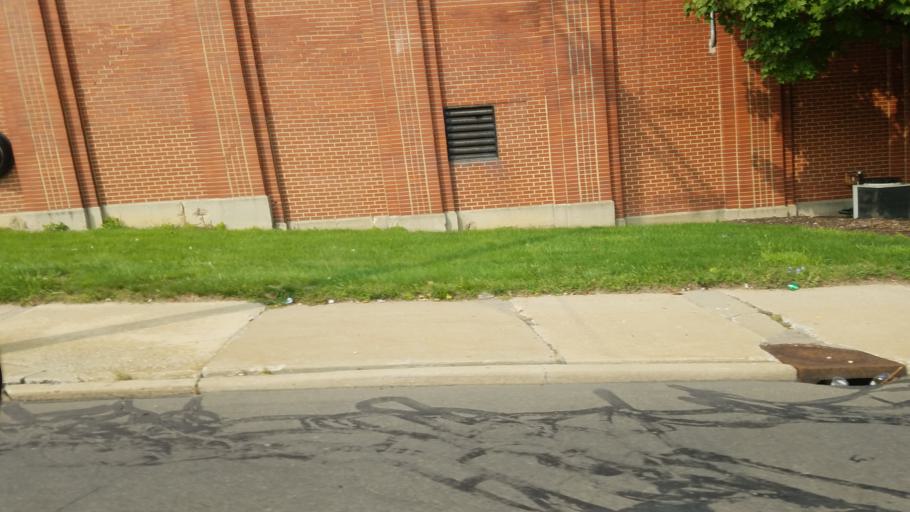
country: US
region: Ohio
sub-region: Mahoning County
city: Youngstown
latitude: 41.0903
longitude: -80.6464
